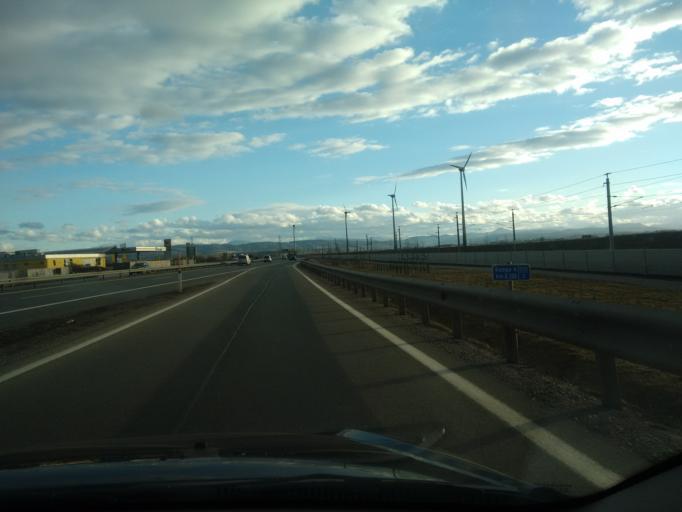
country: AT
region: Lower Austria
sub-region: Sankt Polten Stadt
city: Sankt Poelten
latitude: 48.1976
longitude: 15.6607
